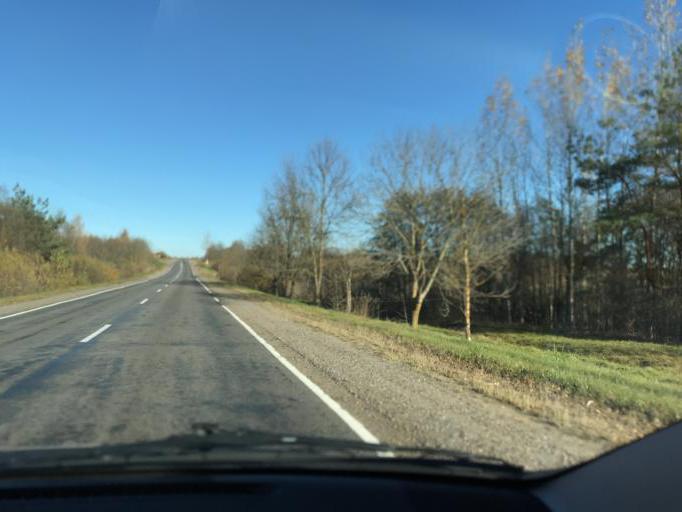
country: BY
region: Vitebsk
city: Lyepyel'
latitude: 55.0275
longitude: 28.7455
